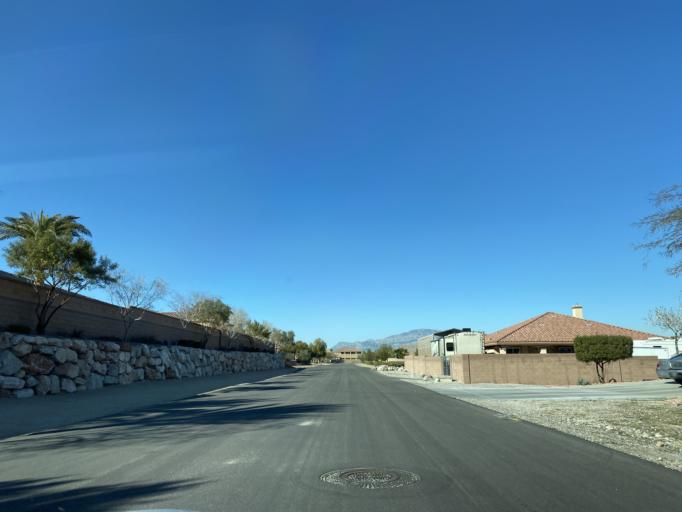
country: US
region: Nevada
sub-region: Clark County
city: Summerlin South
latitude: 36.2928
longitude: -115.3081
